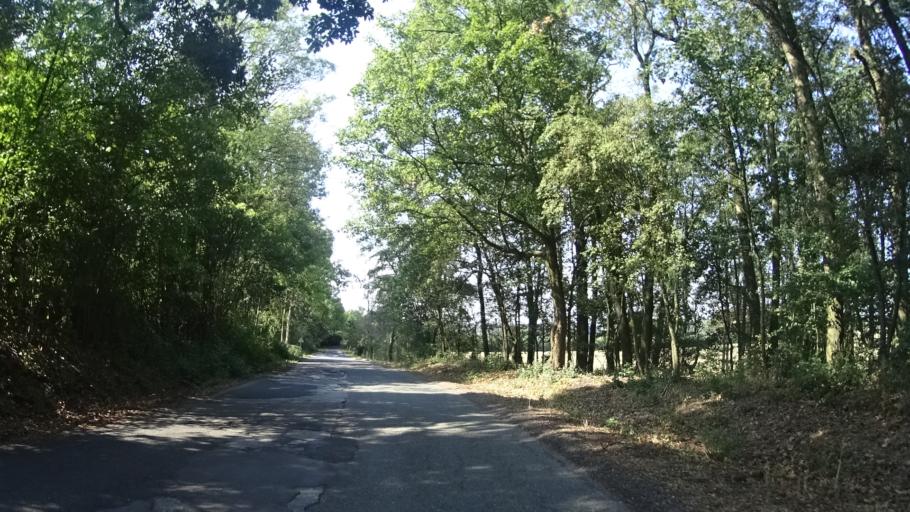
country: CZ
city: Smidary
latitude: 50.2795
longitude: 15.5238
